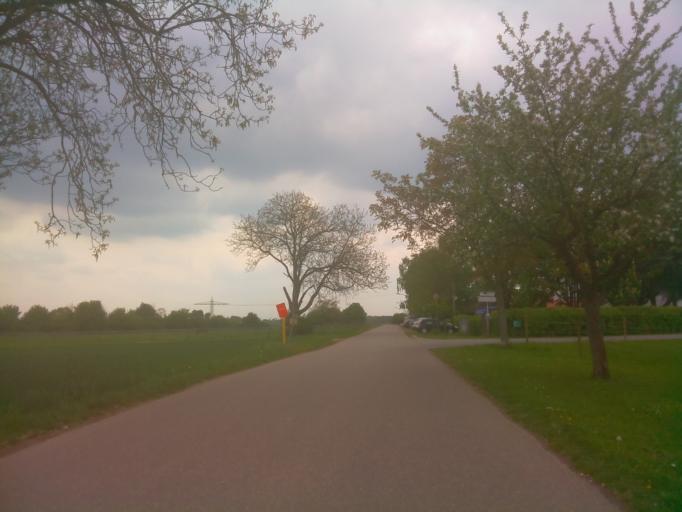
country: DE
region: Baden-Wuerttemberg
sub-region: Karlsruhe Region
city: Eppelheim
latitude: 49.3929
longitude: 8.6226
